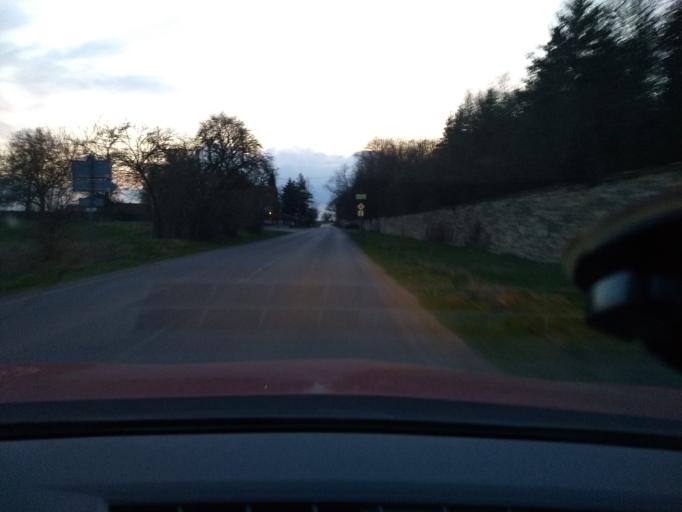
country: CZ
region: Central Bohemia
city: Jenec
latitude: 50.0681
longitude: 14.1873
